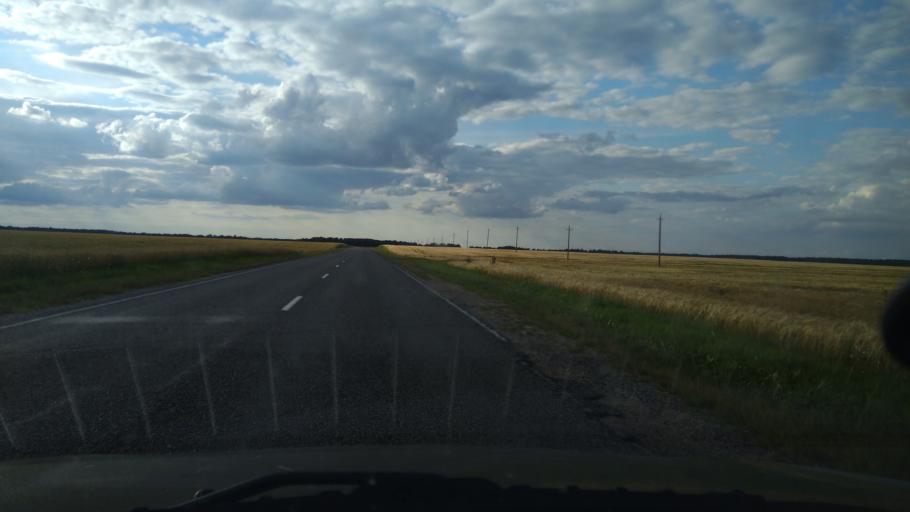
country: BY
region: Grodnenskaya
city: Masty
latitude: 53.3288
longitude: 24.6782
